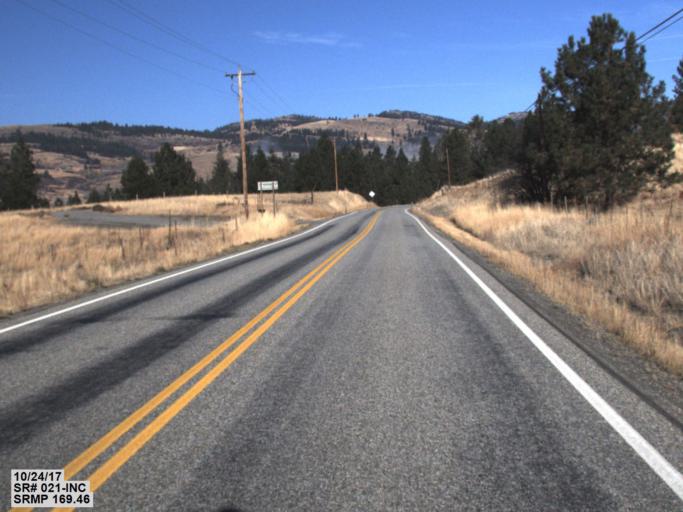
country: US
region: Washington
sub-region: Ferry County
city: Republic
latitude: 48.7357
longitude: -118.6595
